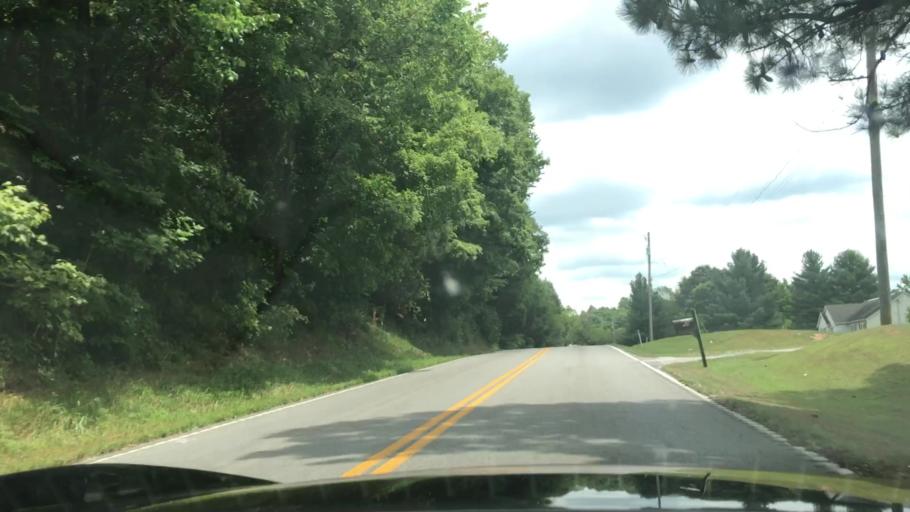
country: US
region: Kentucky
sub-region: Muhlenberg County
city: Greenville
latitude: 37.2031
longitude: -87.0907
